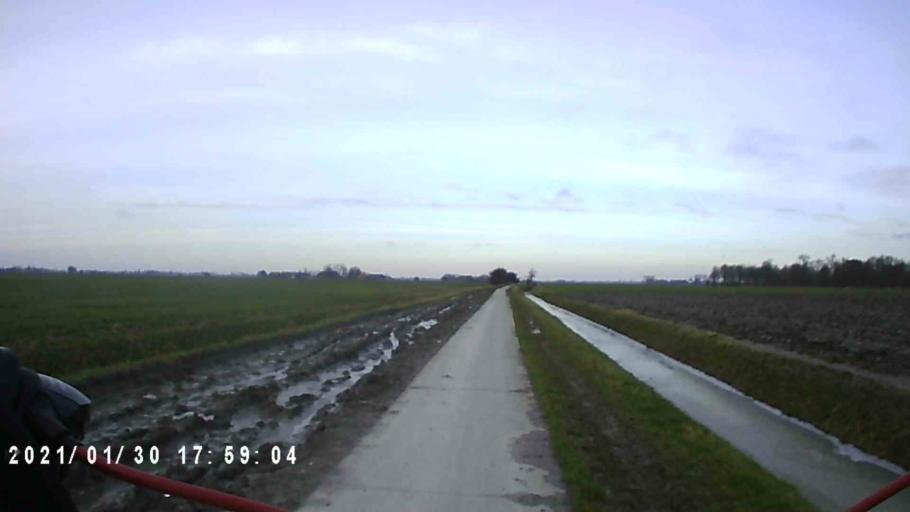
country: NL
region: Groningen
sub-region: Gemeente Zuidhorn
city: Noordhorn
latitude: 53.2745
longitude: 6.4130
